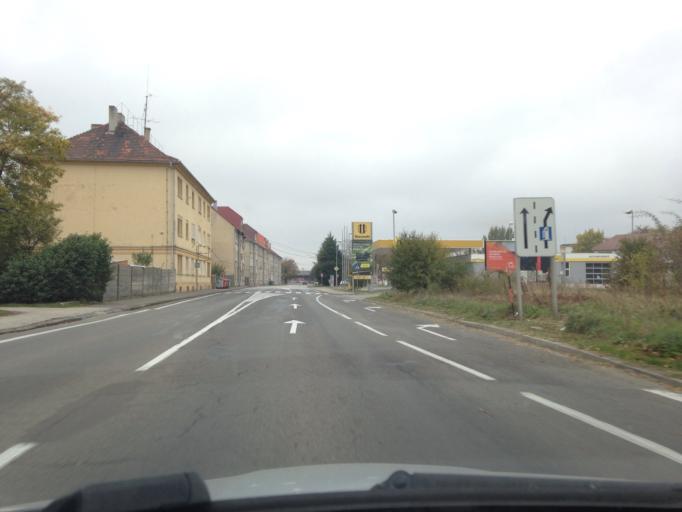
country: SK
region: Nitriansky
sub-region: Okres Nove Zamky
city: Sturovo
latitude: 47.7988
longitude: 18.6833
